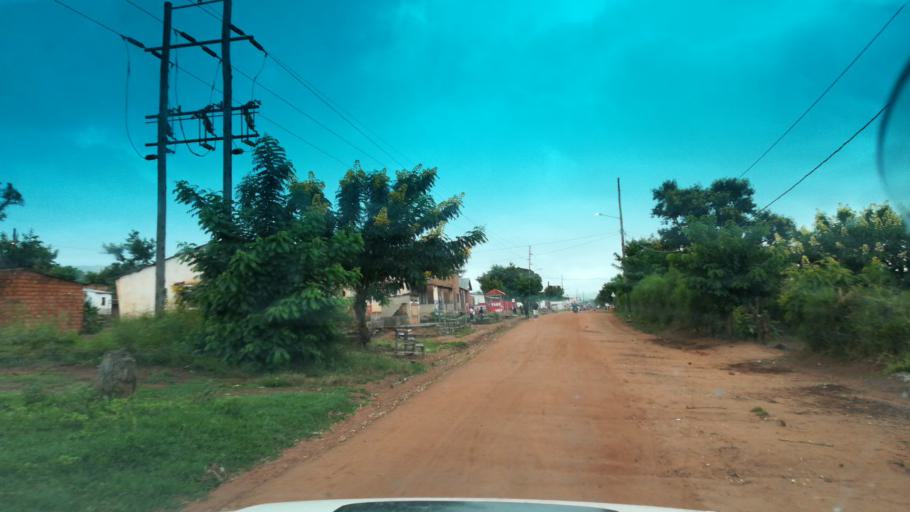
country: ZM
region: Northern
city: Kaputa
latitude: -8.4707
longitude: 28.8972
